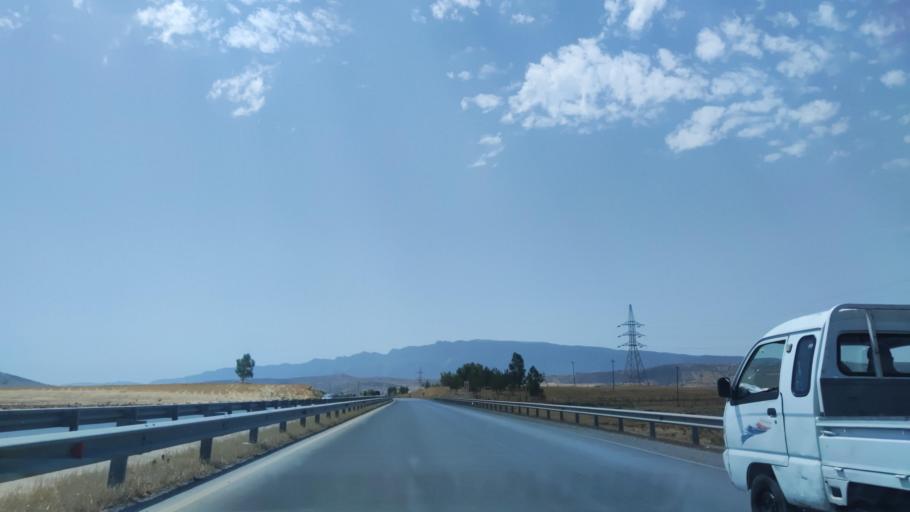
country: IQ
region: Arbil
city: Shaqlawah
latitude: 36.4800
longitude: 44.3806
